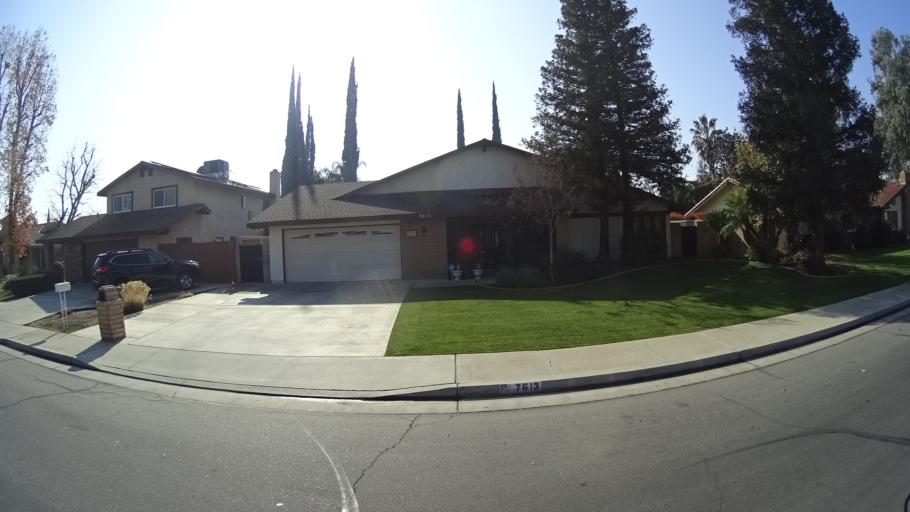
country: US
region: California
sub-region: Kern County
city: Greenacres
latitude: 35.3610
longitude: -119.0872
